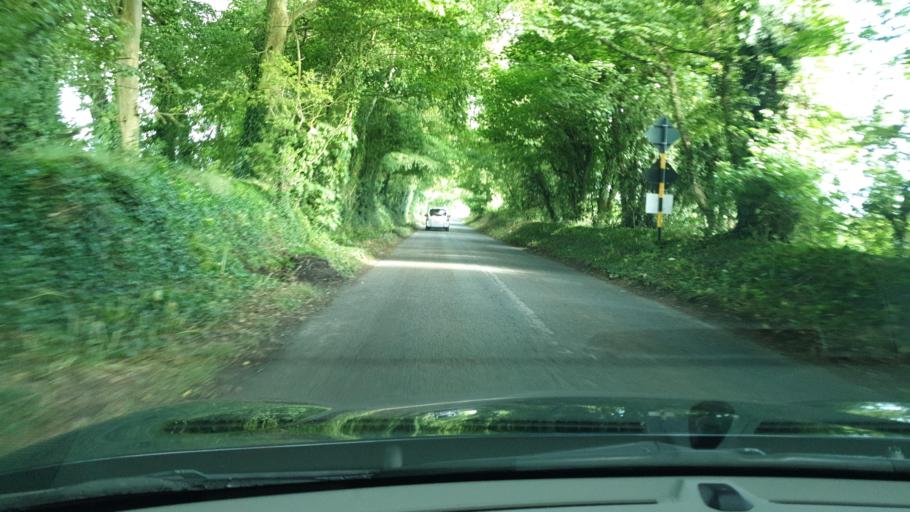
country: IE
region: Leinster
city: Balrothery
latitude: 53.5692
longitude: -6.1526
